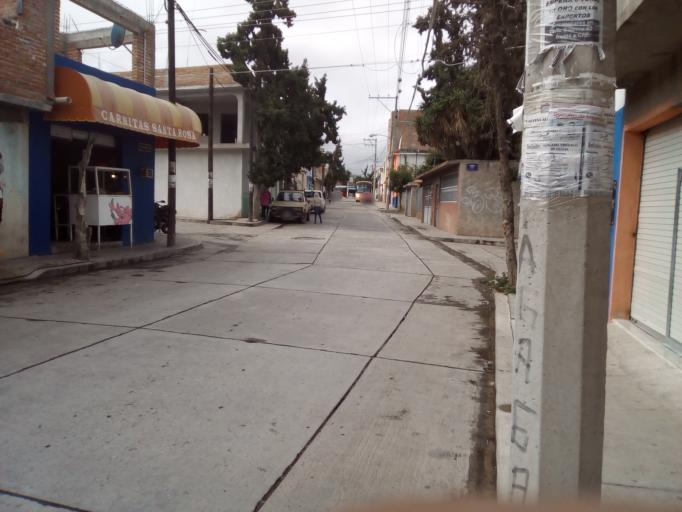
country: MX
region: Guerrero
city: San Luis de la Paz
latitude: 21.2914
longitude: -100.5118
